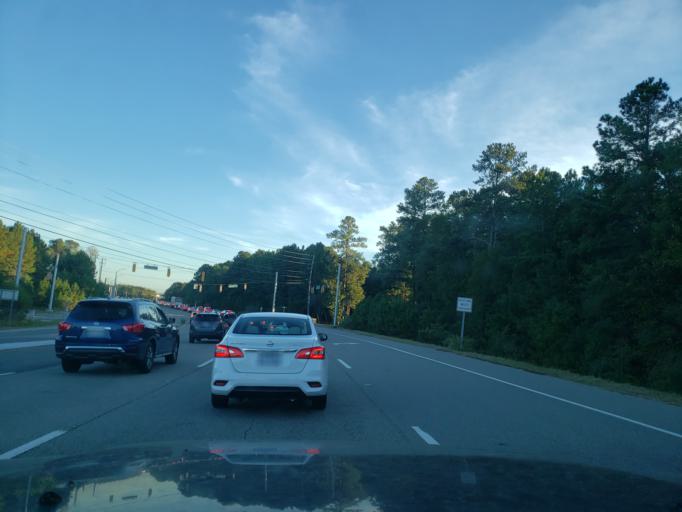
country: US
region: North Carolina
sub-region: Wake County
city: Morrisville
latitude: 35.8296
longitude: -78.8530
